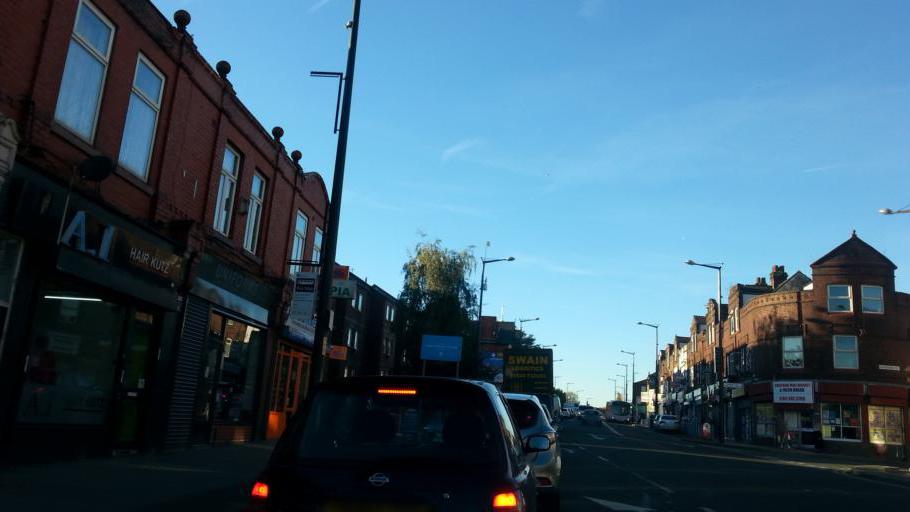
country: GB
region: England
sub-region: Manchester
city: Crumpsall
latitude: 53.5086
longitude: -2.2422
